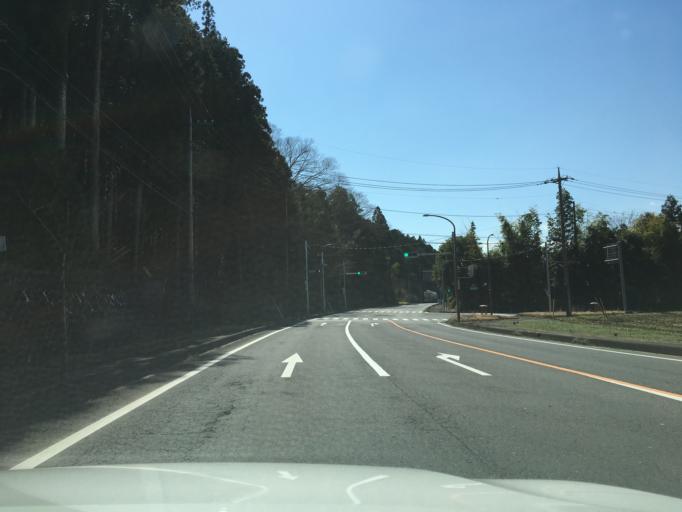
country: JP
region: Tochigi
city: Kuroiso
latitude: 36.9449
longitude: 140.1448
